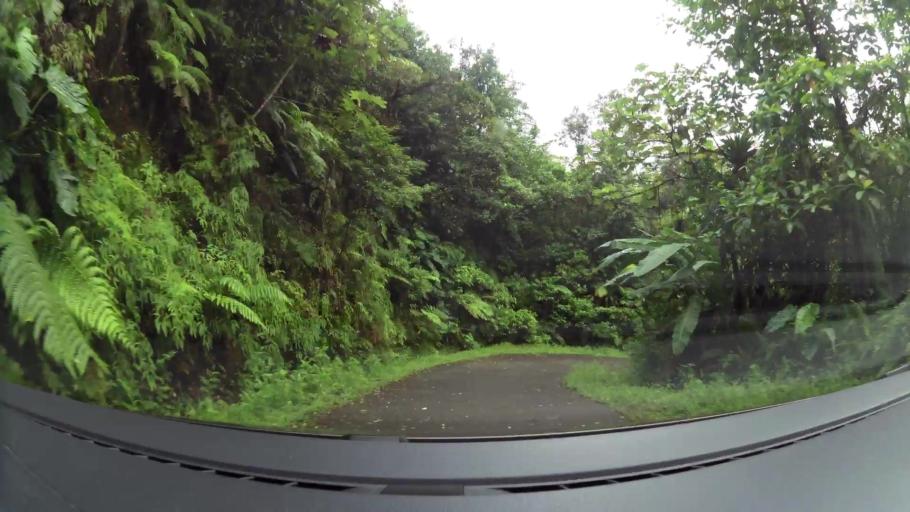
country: GP
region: Guadeloupe
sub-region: Guadeloupe
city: Trois-Rivieres
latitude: 16.0371
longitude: -61.6384
